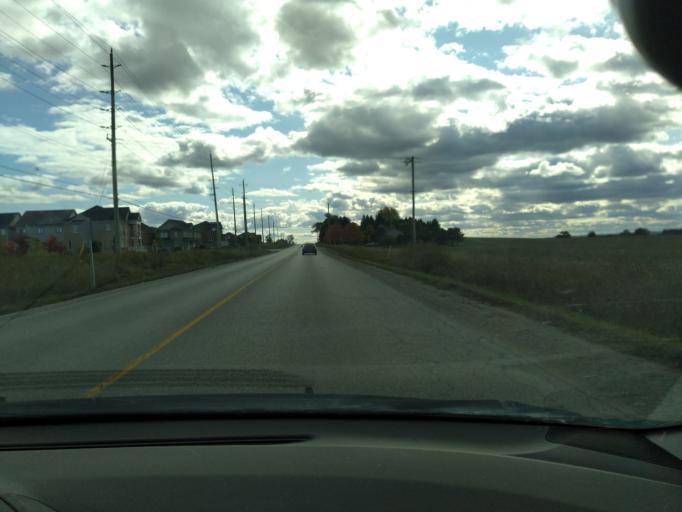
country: CA
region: Ontario
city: Bradford West Gwillimbury
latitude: 44.1037
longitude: -79.6012
